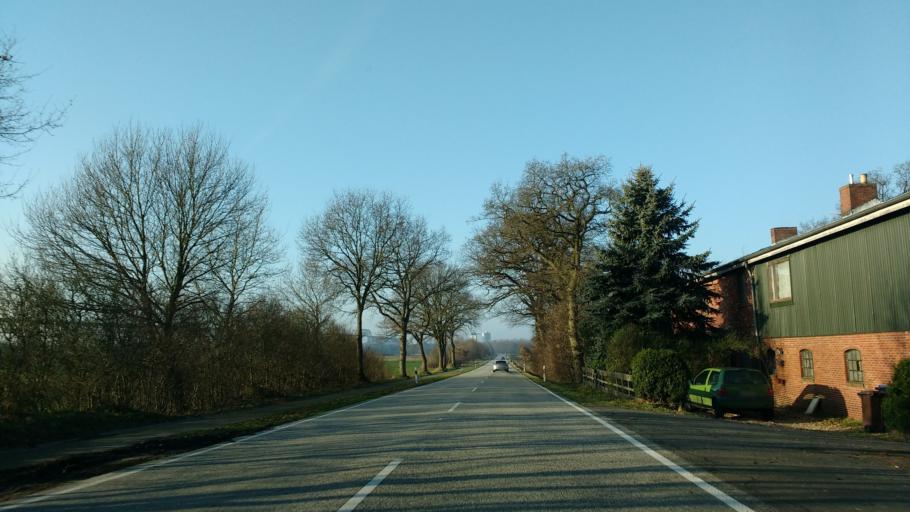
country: DE
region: Schleswig-Holstein
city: Gribbohm
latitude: 54.0177
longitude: 9.3224
